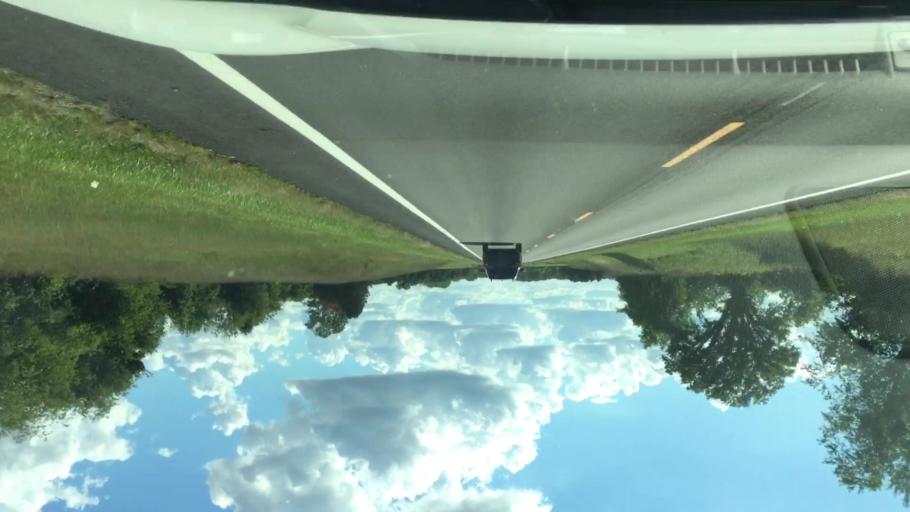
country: US
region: Ohio
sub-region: Clark County
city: Northridge
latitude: 39.9771
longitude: -83.7587
